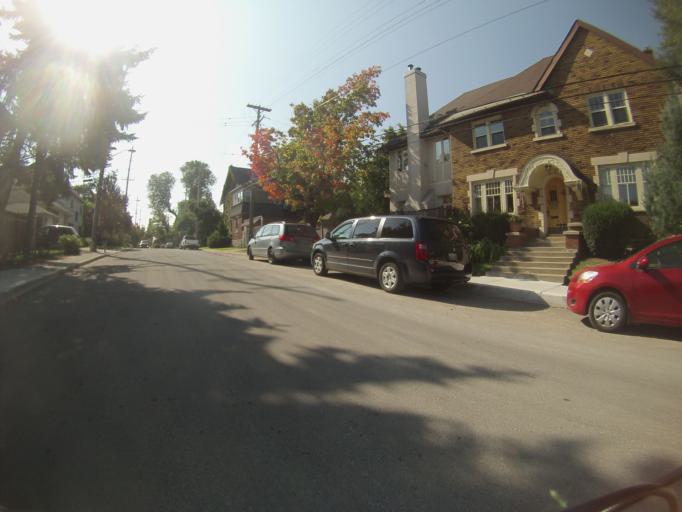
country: CA
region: Ontario
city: Ottawa
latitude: 45.4058
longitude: -75.6941
